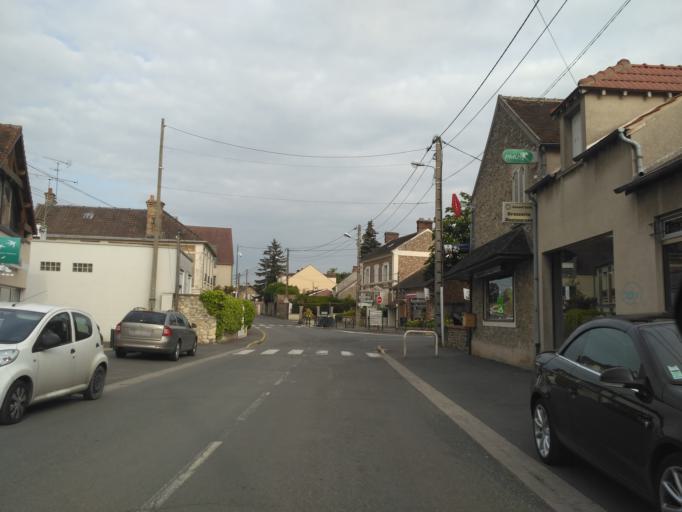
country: FR
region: Ile-de-France
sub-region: Departement de Seine-et-Marne
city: Cesson
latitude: 48.5630
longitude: 2.6031
